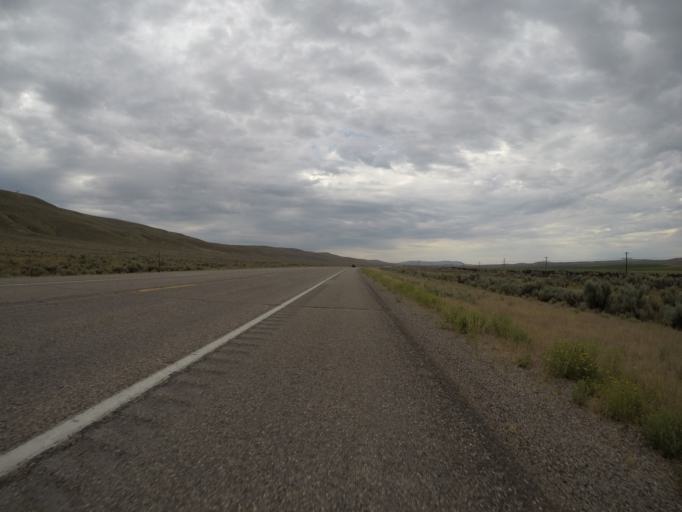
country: US
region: Utah
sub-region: Rich County
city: Randolph
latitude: 41.8522
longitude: -110.9723
